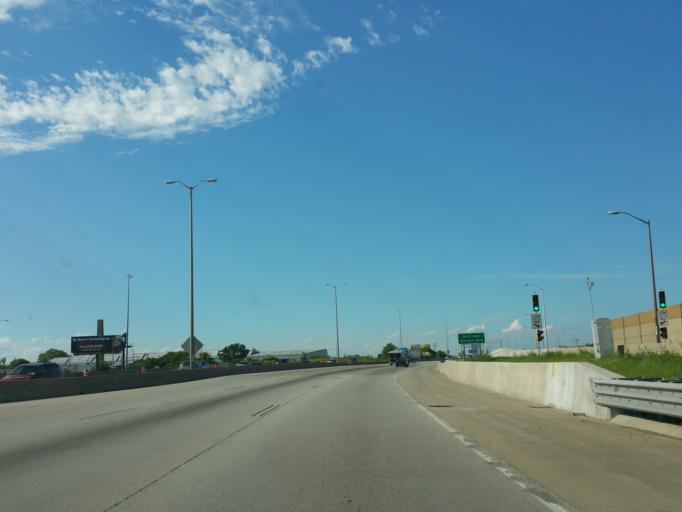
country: US
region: Wisconsin
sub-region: Milwaukee County
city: Saint Francis
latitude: 42.9813
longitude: -87.9165
